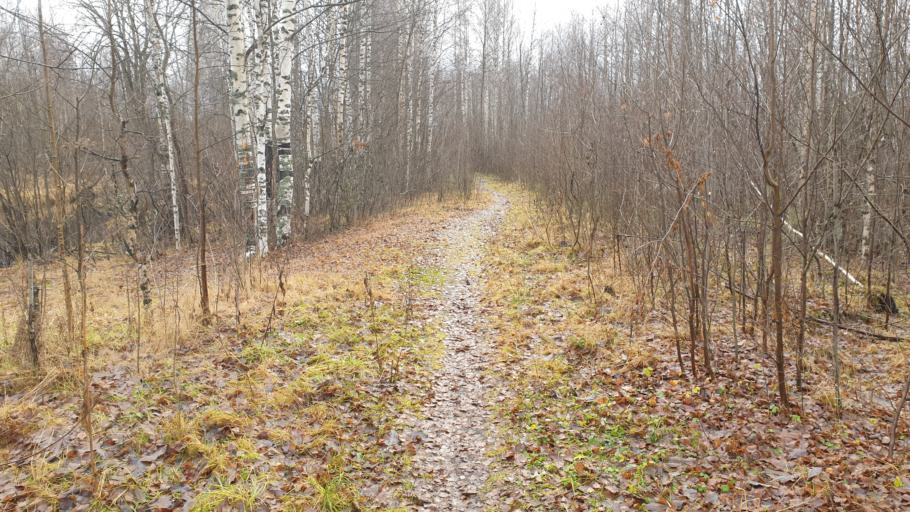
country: RU
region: Kirov
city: Kirs
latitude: 59.3335
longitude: 52.2382
